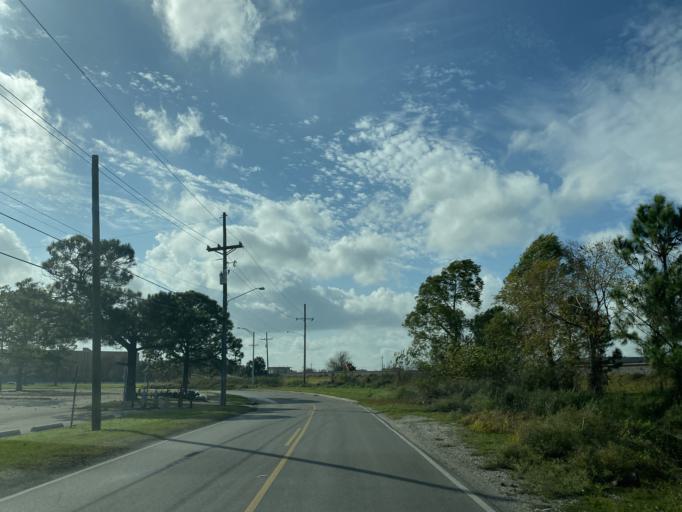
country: US
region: Louisiana
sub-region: Orleans Parish
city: New Orleans
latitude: 30.0289
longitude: -90.0429
